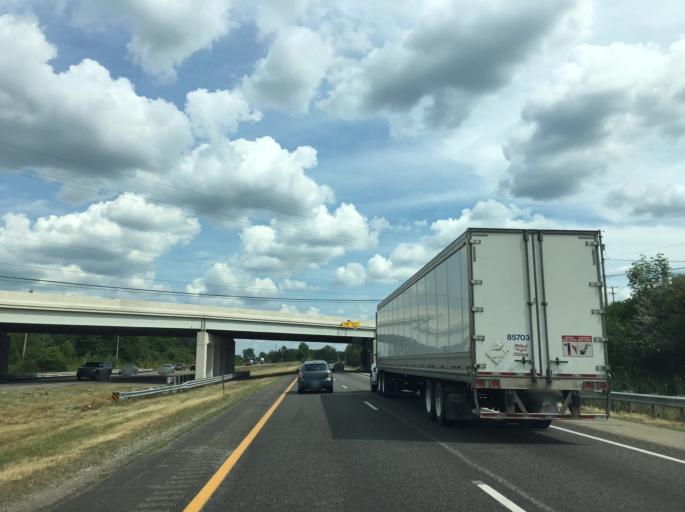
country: US
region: Michigan
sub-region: Genesee County
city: Grand Blanc
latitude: 42.9287
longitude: -83.6921
